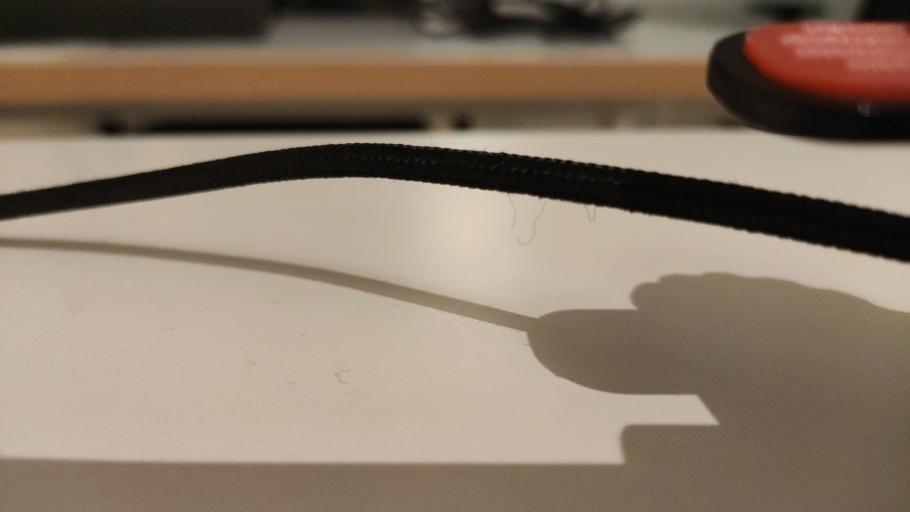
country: RU
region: Moskovskaya
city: Il'inskiy Pogost
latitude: 55.5222
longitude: 38.8719
